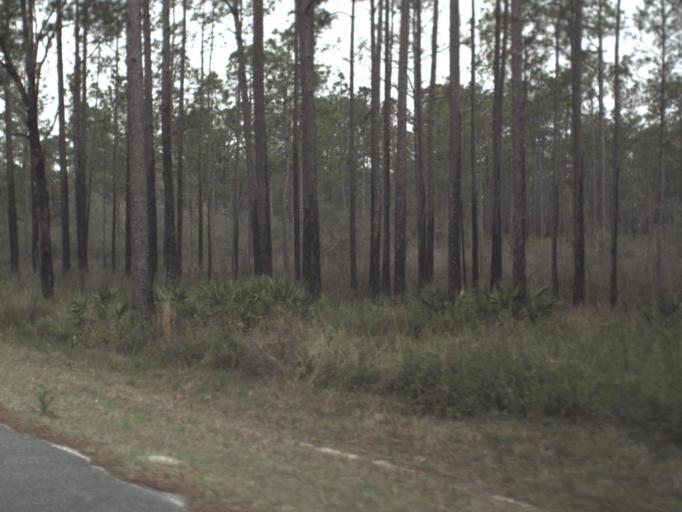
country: US
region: Florida
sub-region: Franklin County
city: Apalachicola
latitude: 29.9276
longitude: -84.9771
